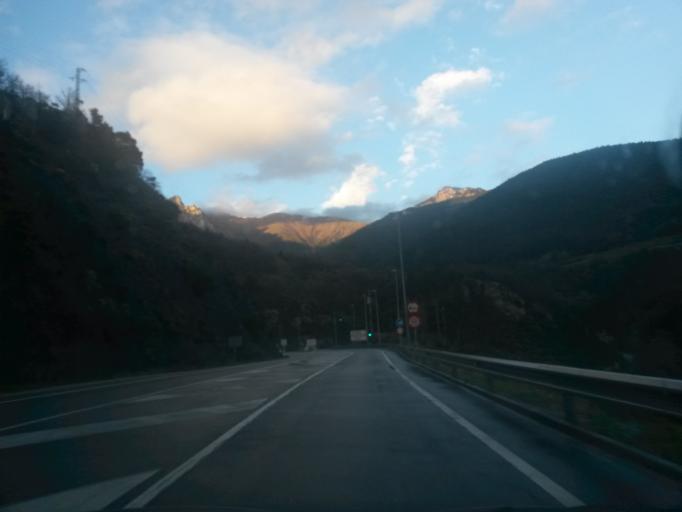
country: ES
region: Catalonia
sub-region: Provincia de Barcelona
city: Baga
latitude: 42.2935
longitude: 1.8610
